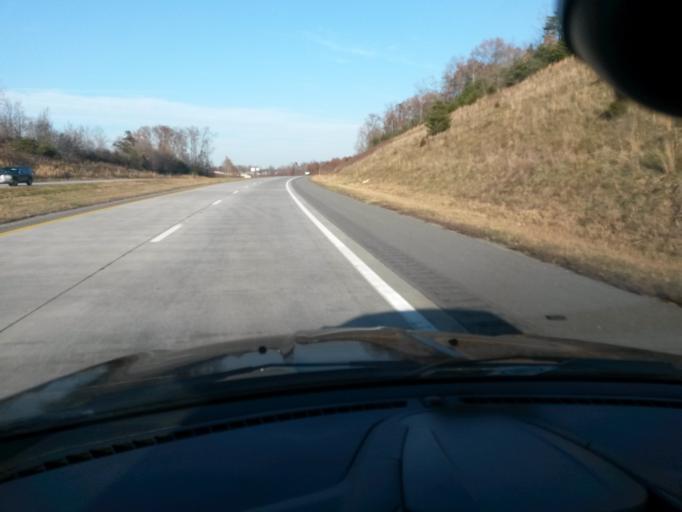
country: US
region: Virginia
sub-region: Amherst County
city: Madison Heights
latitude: 37.4741
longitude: -79.0804
